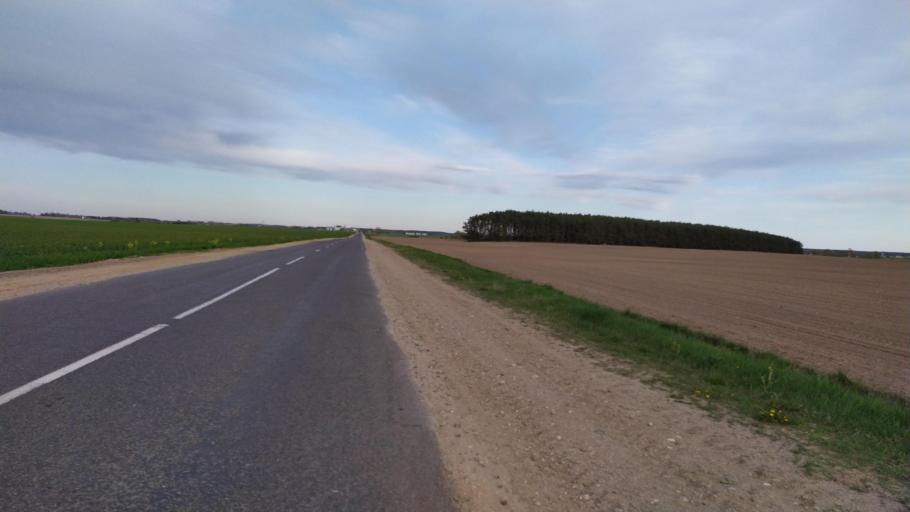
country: BY
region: Brest
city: Kamyanyets
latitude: 52.4080
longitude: 23.7378
